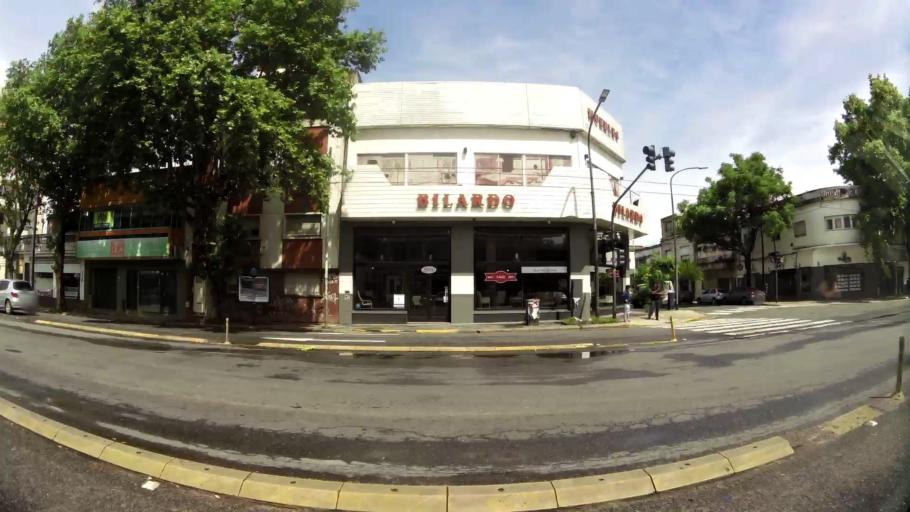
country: AR
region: Buenos Aires F.D.
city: Villa Santa Rita
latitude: -34.6118
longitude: -58.4689
